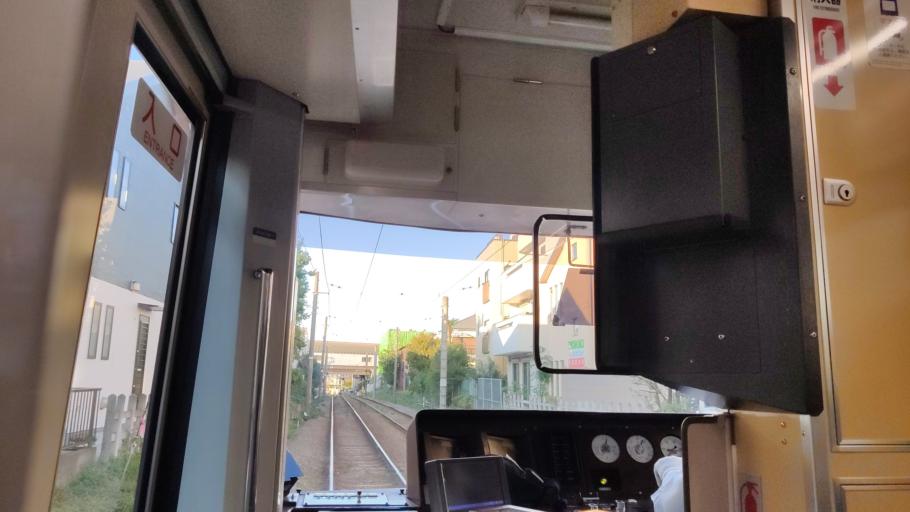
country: JP
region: Tokyo
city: Tokyo
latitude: 35.6518
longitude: 139.6461
